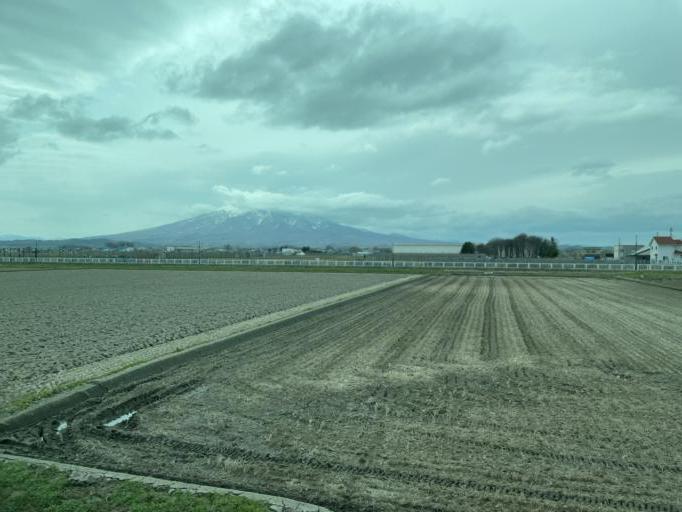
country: JP
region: Aomori
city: Goshogawara
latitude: 40.7454
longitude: 140.4341
